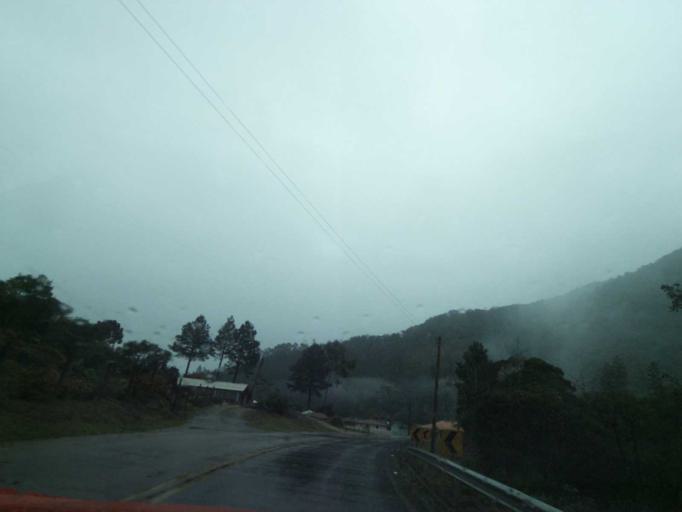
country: BR
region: Santa Catarina
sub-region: Anitapolis
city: Anitapolis
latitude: -27.8338
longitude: -49.0518
